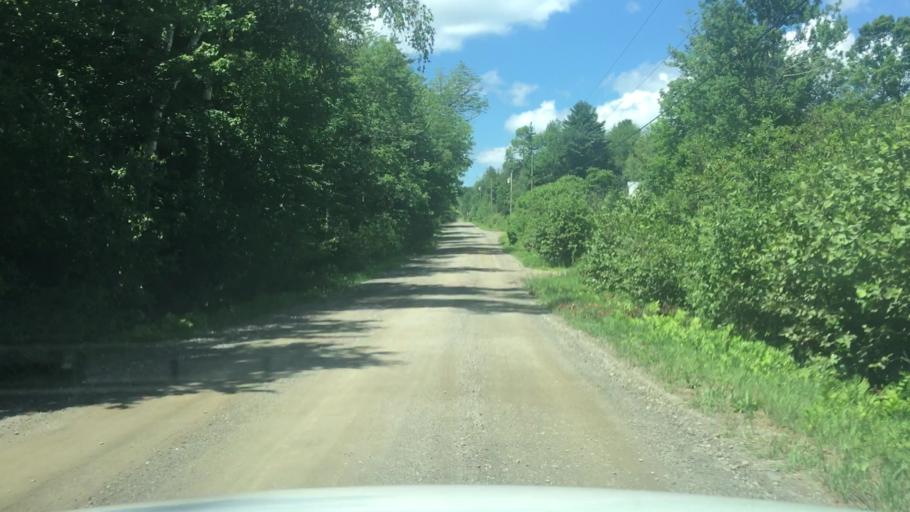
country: US
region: Maine
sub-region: Waldo County
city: Northport
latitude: 44.3457
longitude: -68.9640
